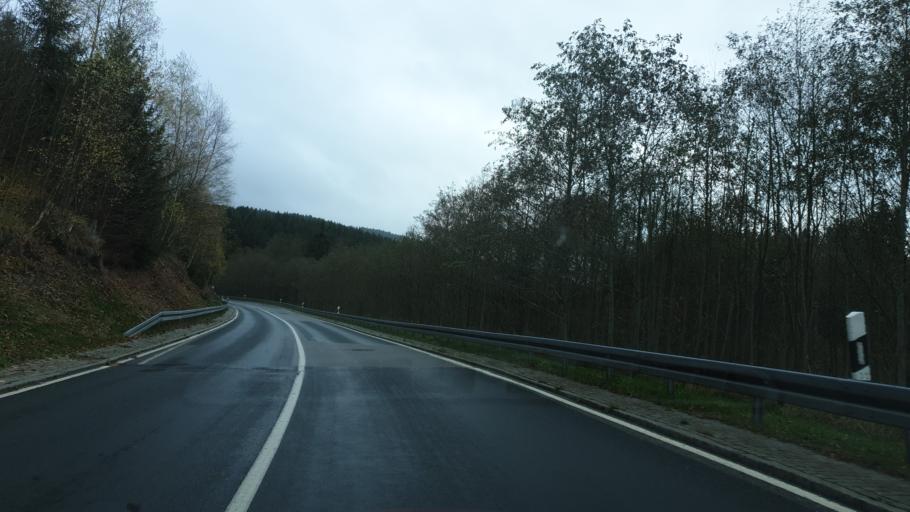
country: DE
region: Saxony
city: Schoenheide
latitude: 50.4925
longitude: 12.5447
